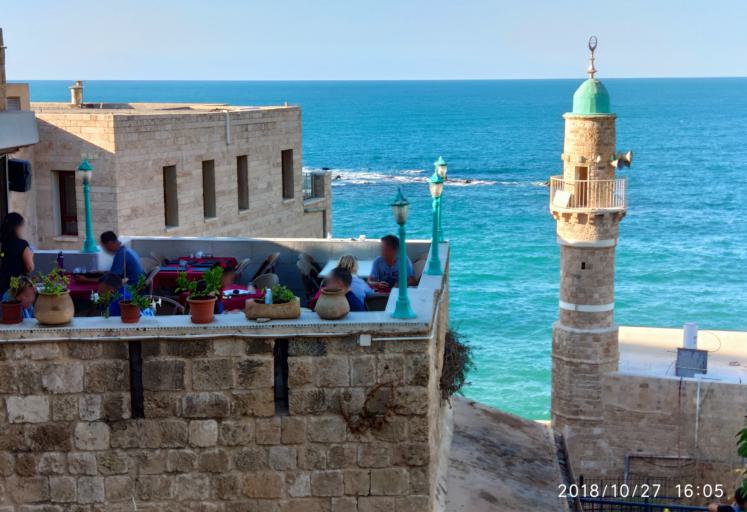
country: IL
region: Tel Aviv
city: Yafo
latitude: 32.0550
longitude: 34.7529
